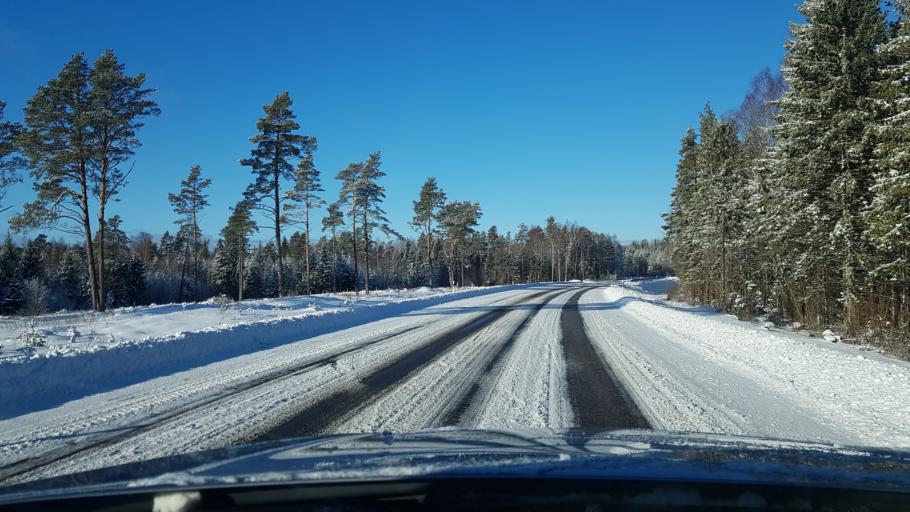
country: EE
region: Hiiumaa
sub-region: Kaerdla linn
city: Kardla
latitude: 58.9698
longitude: 22.7695
